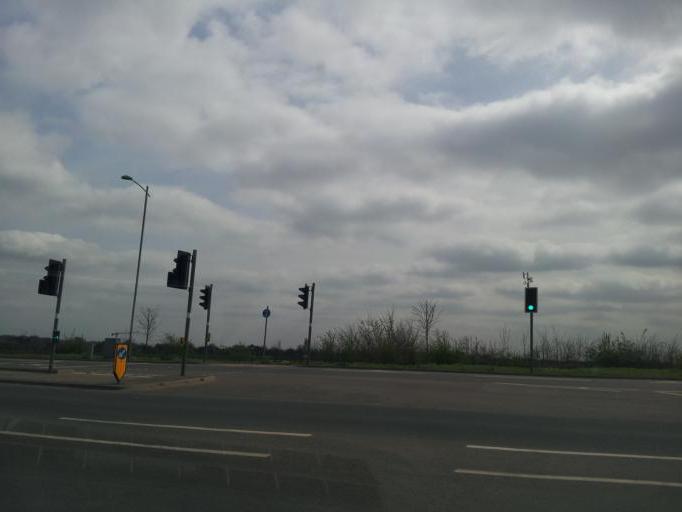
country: GB
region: England
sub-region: Cambridgeshire
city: Grantchester
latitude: 52.1653
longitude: 0.1125
